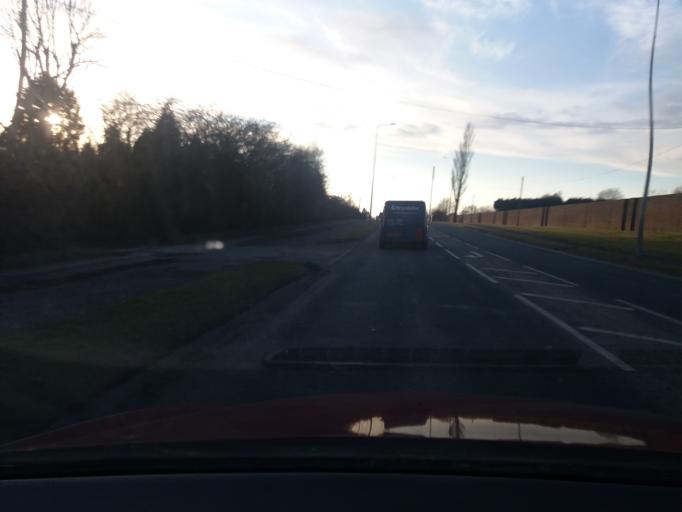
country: GB
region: England
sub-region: Lancashire
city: Euxton
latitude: 53.6702
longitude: -2.6515
